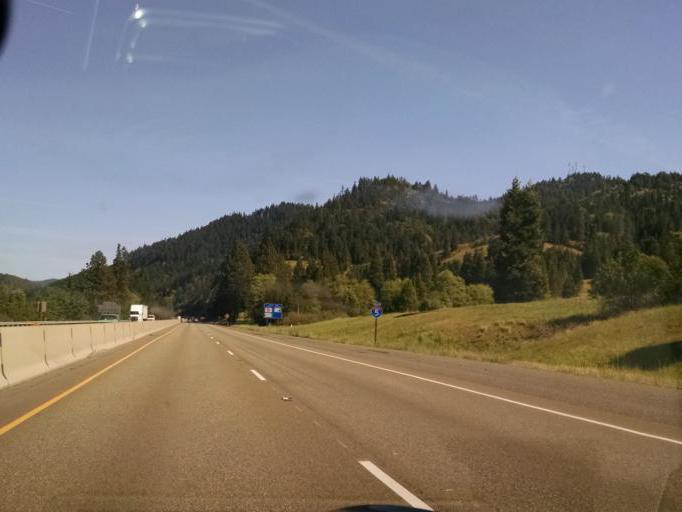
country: US
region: Oregon
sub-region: Douglas County
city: Myrtle Creek
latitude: 43.0342
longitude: -123.3282
